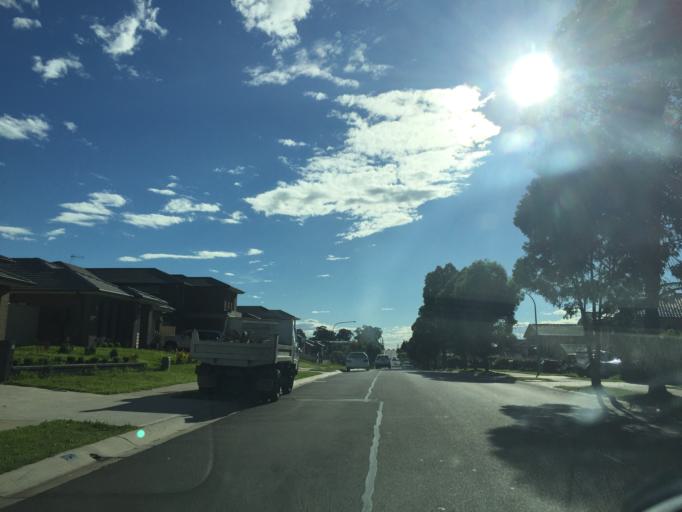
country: AU
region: New South Wales
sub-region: The Hills Shire
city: Beaumont Hills
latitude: -33.7107
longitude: 150.9697
